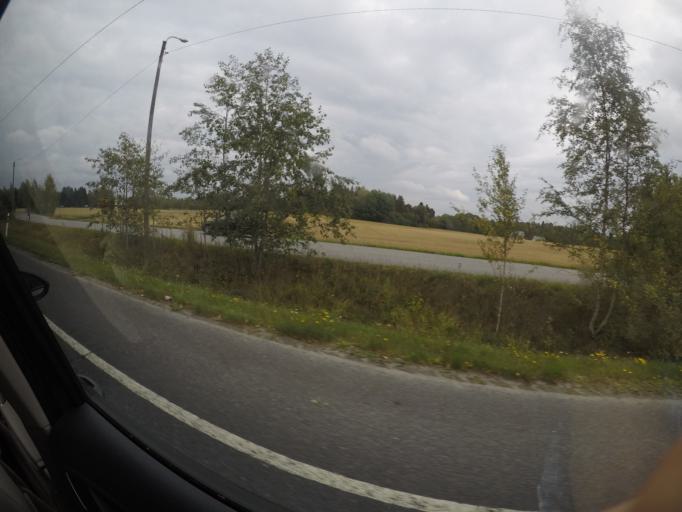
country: FI
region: Haeme
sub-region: Haemeenlinna
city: Parola
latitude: 61.0587
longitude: 24.3925
